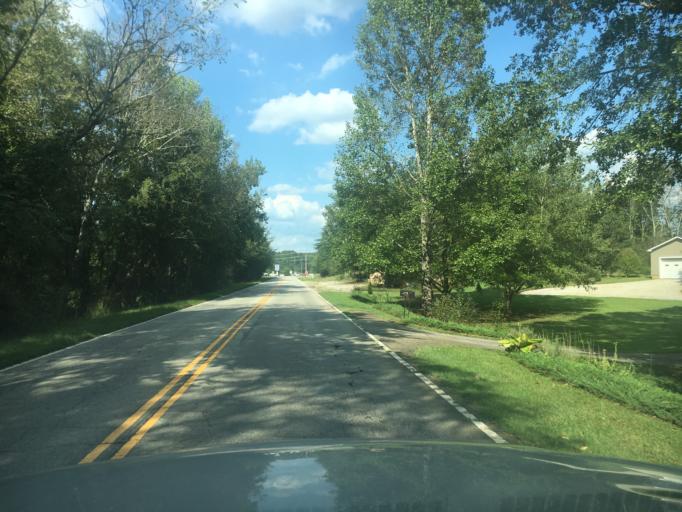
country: US
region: South Carolina
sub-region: Pickens County
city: Central
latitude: 34.6918
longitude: -82.7455
